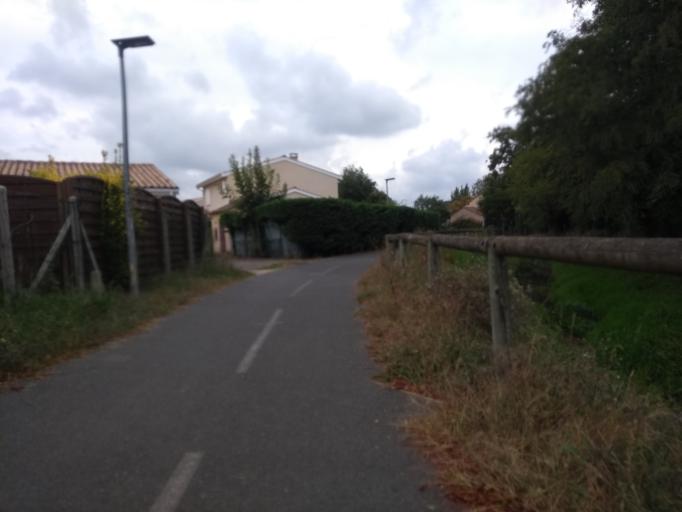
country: FR
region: Aquitaine
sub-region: Departement de la Gironde
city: Merignac
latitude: 44.8262
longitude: -0.6471
